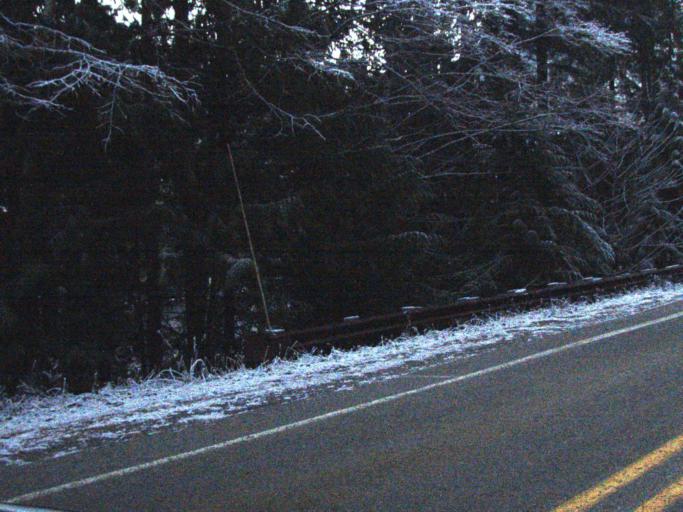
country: US
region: Washington
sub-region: Snohomish County
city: Darrington
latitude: 48.6965
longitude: -121.1097
